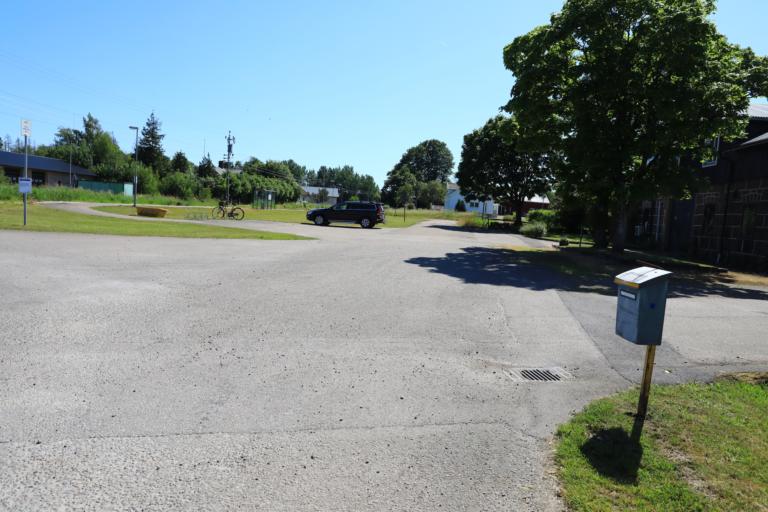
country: SE
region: Halland
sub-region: Varbergs Kommun
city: Varberg
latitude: 57.1739
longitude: 12.3003
